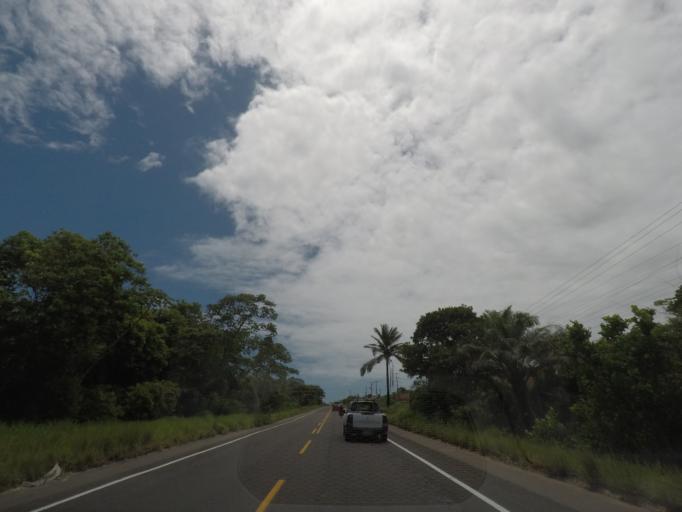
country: BR
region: Bahia
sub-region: Itaparica
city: Itaparica
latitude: -12.9720
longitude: -38.6356
